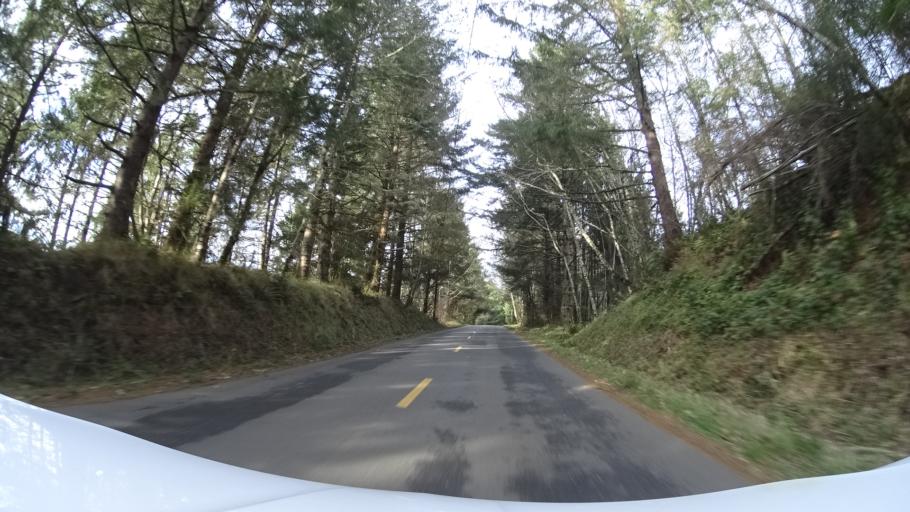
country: US
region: California
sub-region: Humboldt County
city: Ferndale
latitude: 40.5530
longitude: -124.2730
